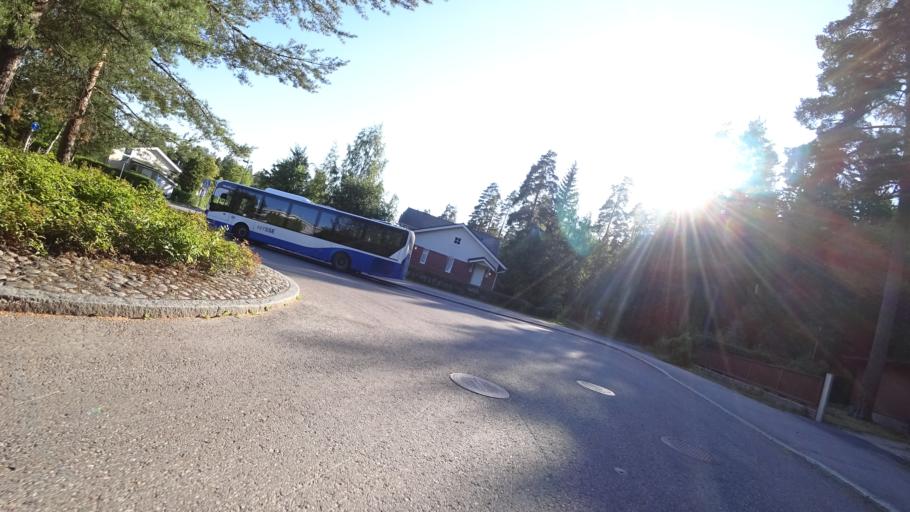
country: FI
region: Pirkanmaa
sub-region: Tampere
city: Pirkkala
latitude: 61.4995
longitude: 23.6168
